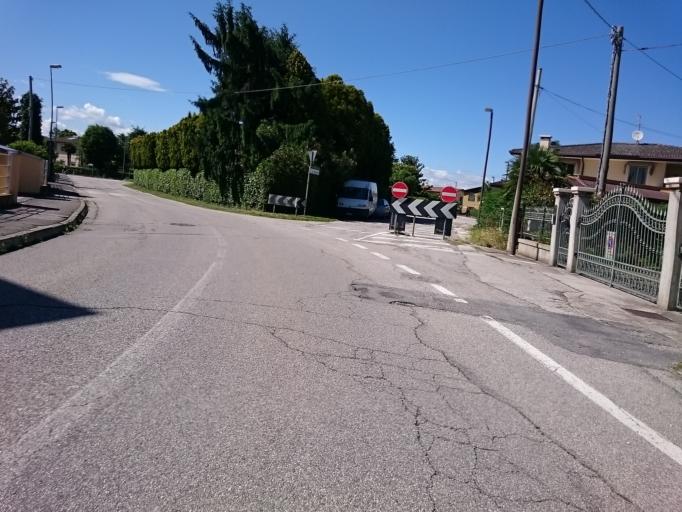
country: IT
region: Veneto
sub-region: Provincia di Padova
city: Piove di Sacco-Piovega
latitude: 45.2904
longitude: 12.0405
